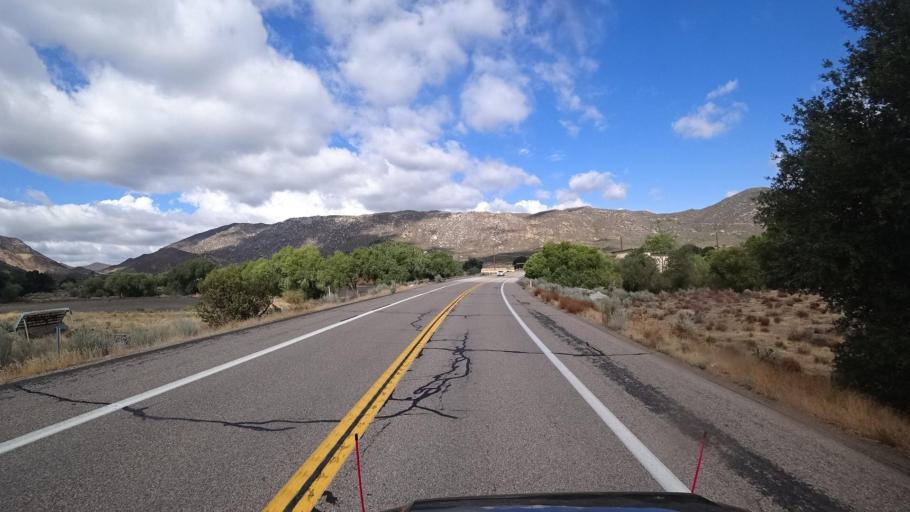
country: US
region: California
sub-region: San Diego County
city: Pine Valley
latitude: 32.7581
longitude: -116.4919
